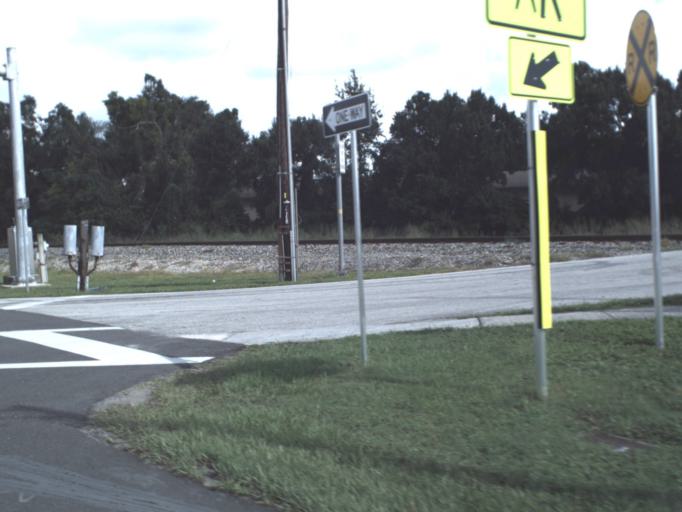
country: US
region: Florida
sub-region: Polk County
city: Lakeland
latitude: 28.0404
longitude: -81.9427
